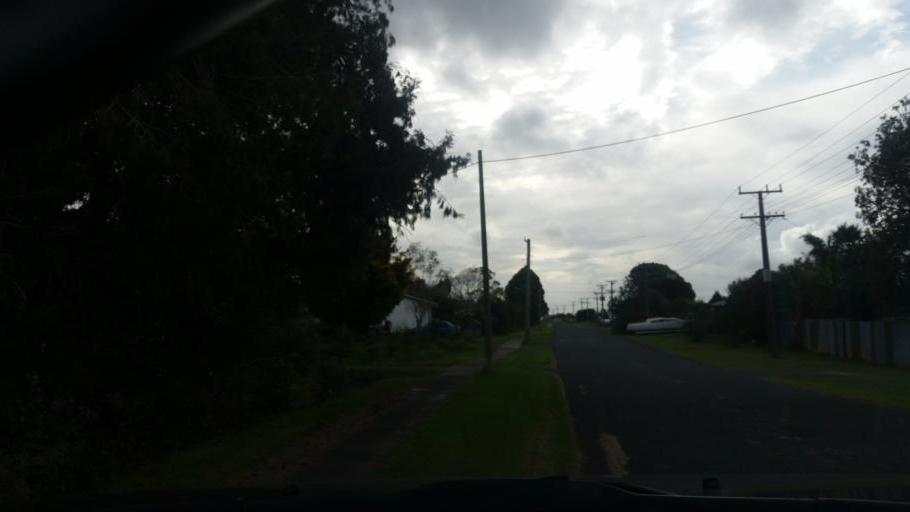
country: NZ
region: Northland
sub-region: Kaipara District
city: Dargaville
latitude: -36.0310
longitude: 173.9174
